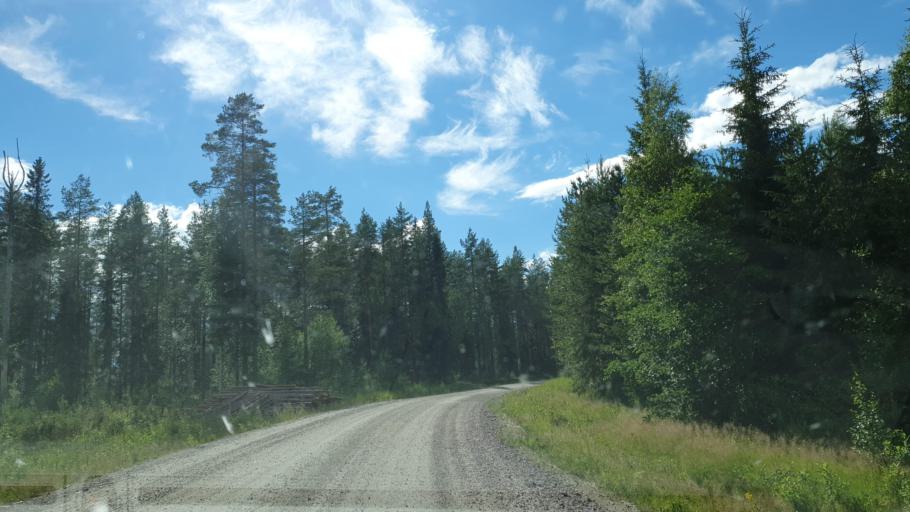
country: FI
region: Kainuu
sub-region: Kehys-Kainuu
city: Kuhmo
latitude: 64.1611
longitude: 29.8343
